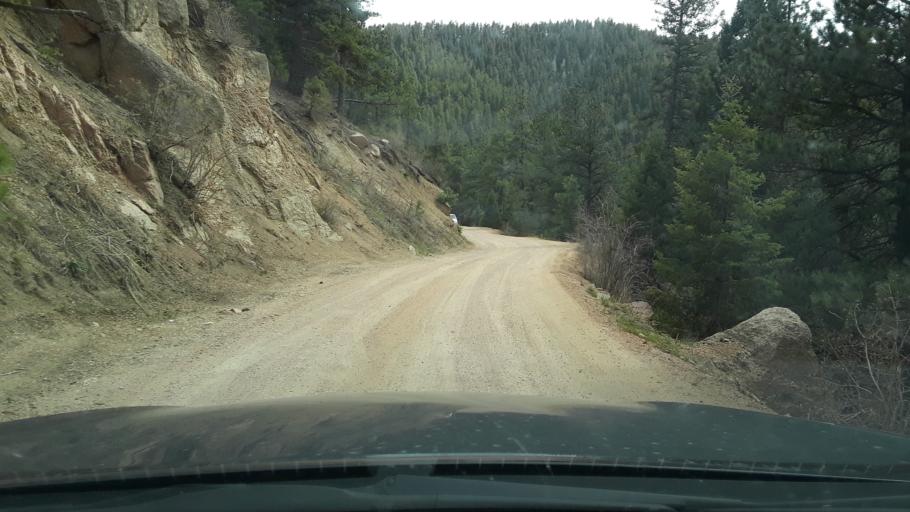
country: US
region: Colorado
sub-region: El Paso County
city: Palmer Lake
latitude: 39.0705
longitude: -104.9323
